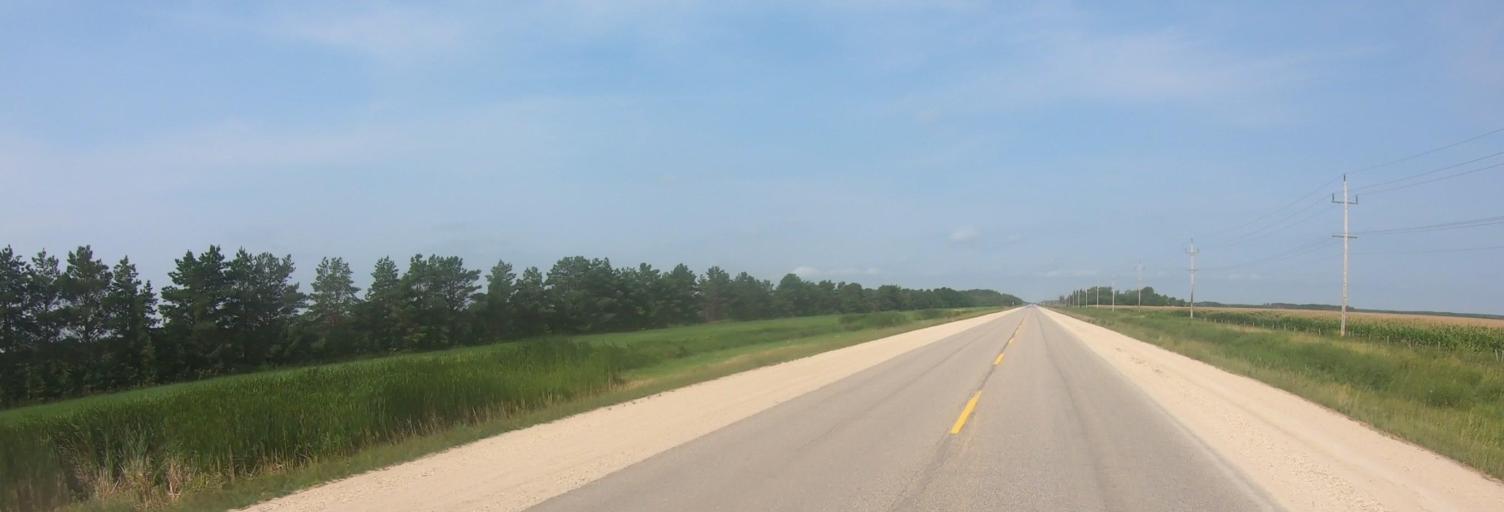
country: CA
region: Manitoba
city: La Broquerie
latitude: 49.3220
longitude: -96.5907
